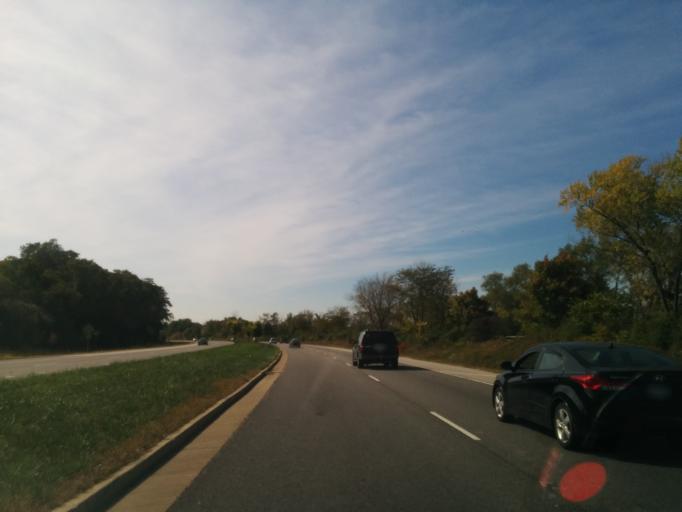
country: US
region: Illinois
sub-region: DuPage County
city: Warrenville
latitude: 41.8300
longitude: -88.1699
